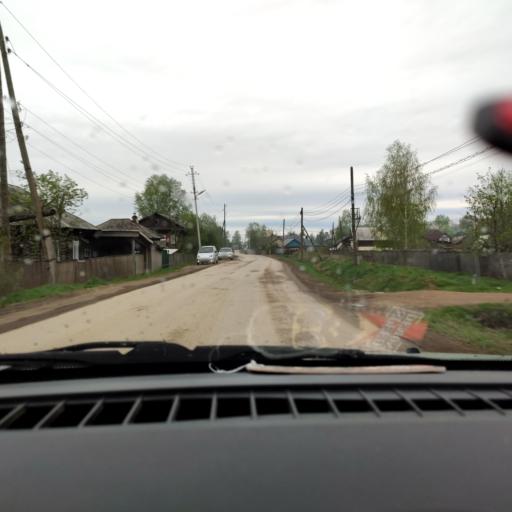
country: RU
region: Perm
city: Kudymkar
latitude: 59.0074
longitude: 54.6746
